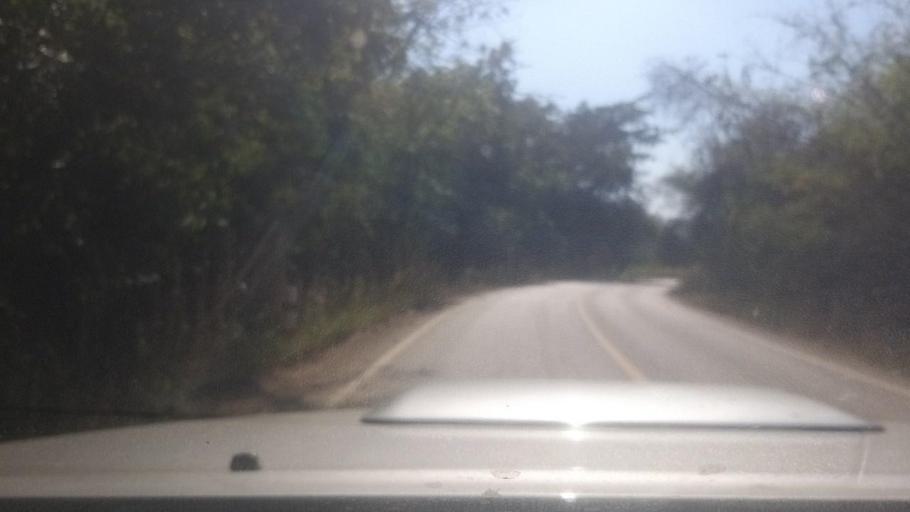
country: TH
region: Phrae
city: Nong Muang Khai
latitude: 18.2939
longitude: 100.0321
